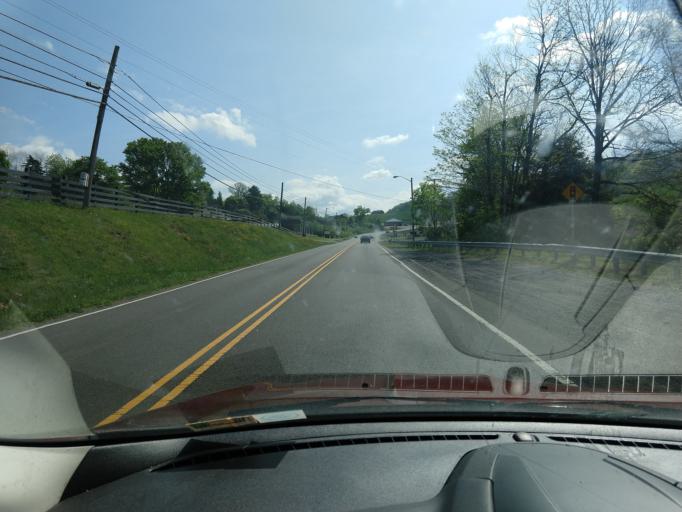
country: US
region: Virginia
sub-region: Russell County
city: Honaker
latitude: 37.0152
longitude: -81.9615
